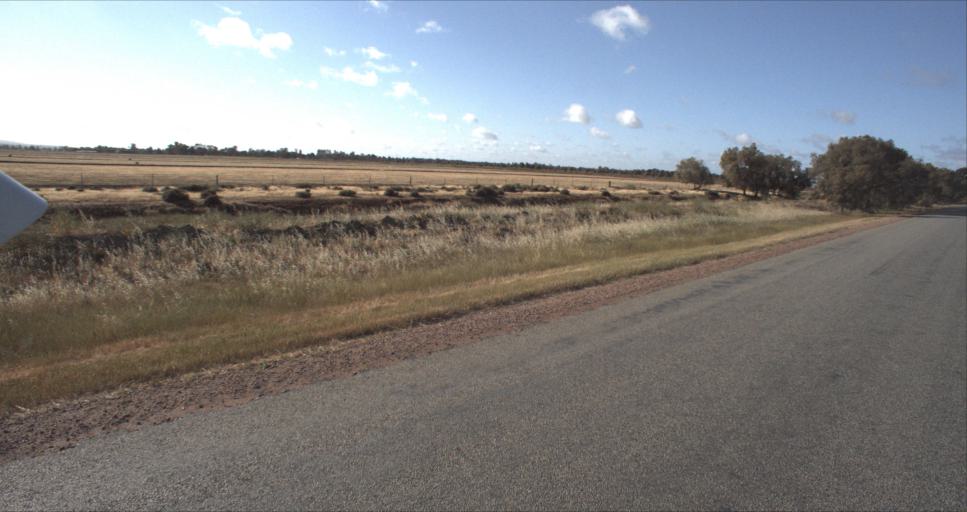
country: AU
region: New South Wales
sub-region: Leeton
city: Leeton
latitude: -34.5136
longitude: 146.3919
